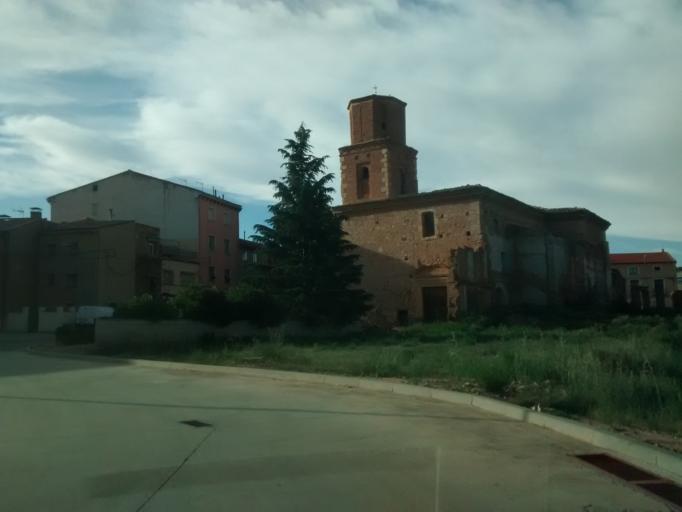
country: ES
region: Aragon
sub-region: Provincia de Zaragoza
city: Ariza
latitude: 41.3122
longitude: -2.0529
